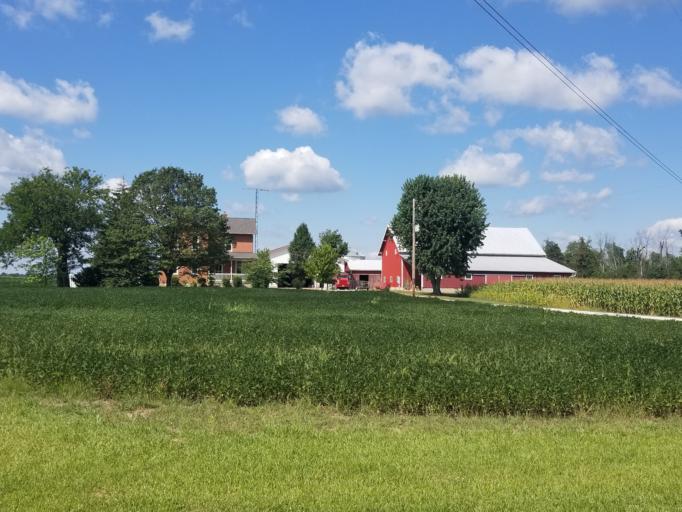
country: US
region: Ohio
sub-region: Wyandot County
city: Carey
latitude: 41.0404
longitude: -83.3245
